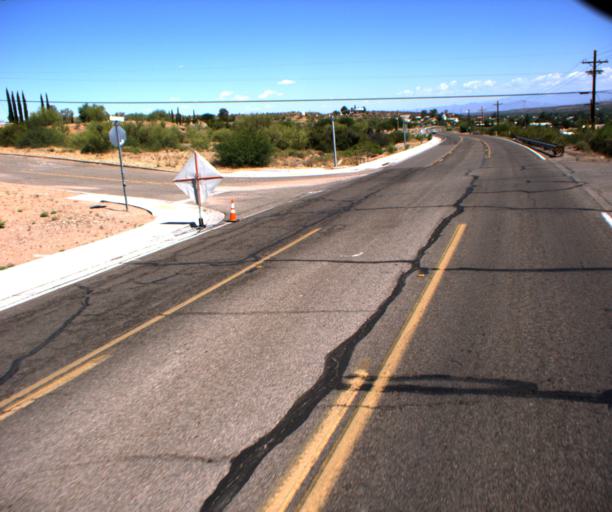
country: US
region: Arizona
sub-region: Pinal County
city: Mammoth
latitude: 32.7155
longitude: -110.6418
